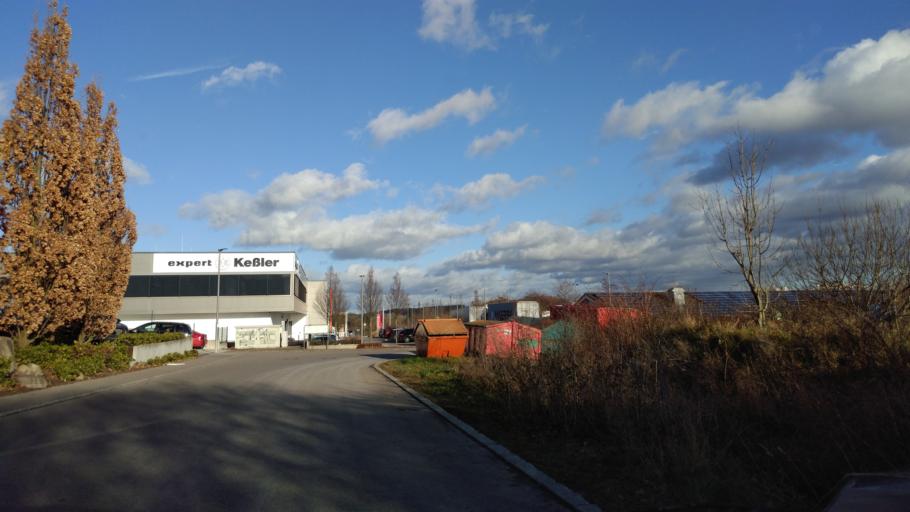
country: DE
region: Baden-Wuerttemberg
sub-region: Tuebingen Region
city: Bad Waldsee
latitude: 47.9133
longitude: 9.7411
